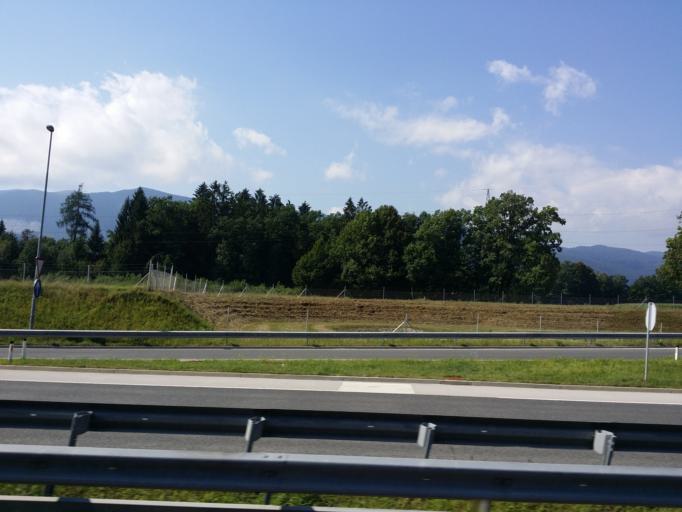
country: SI
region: Radovljica
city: Radovljica
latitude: 46.3376
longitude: 14.1935
